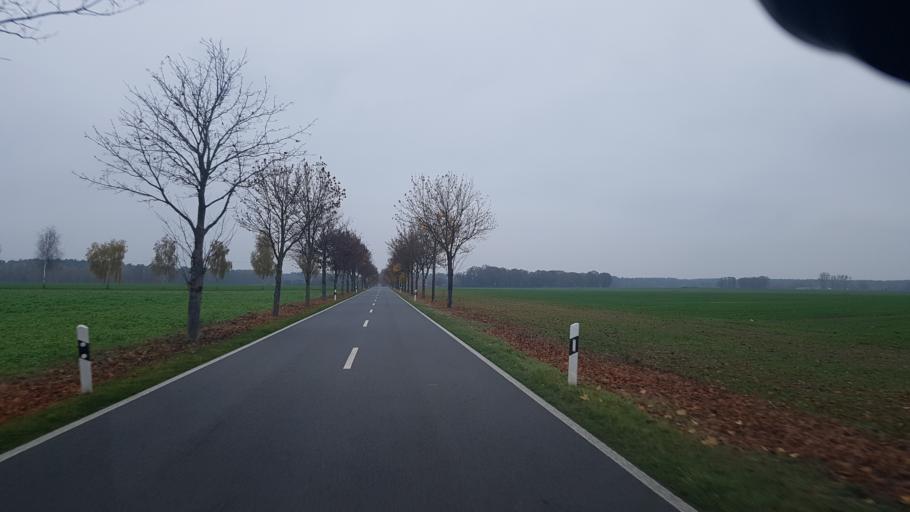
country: DE
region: Brandenburg
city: Lindow
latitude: 52.9439
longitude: 13.0134
